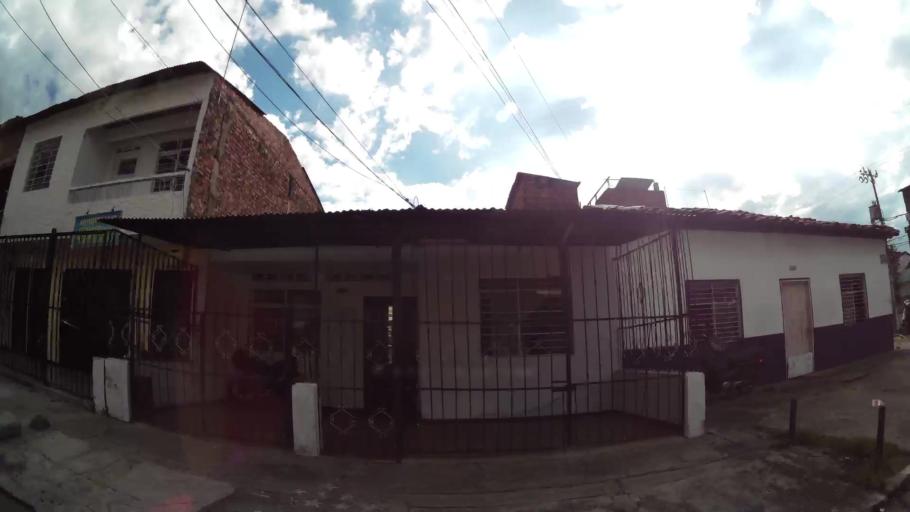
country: CO
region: Valle del Cauca
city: Cali
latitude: 3.4097
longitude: -76.5169
